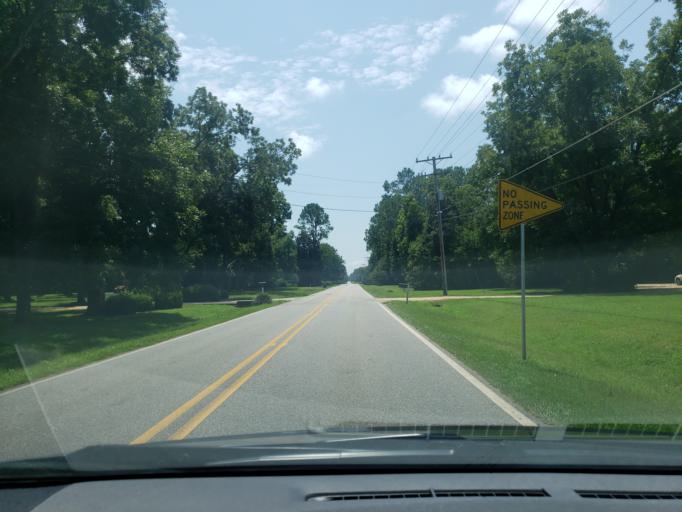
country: US
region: Georgia
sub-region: Dougherty County
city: Albany
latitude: 31.6105
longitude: -84.2750
